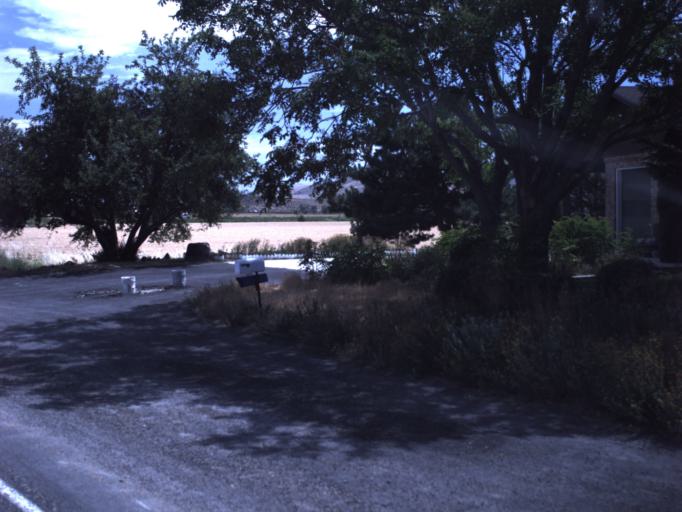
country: US
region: Utah
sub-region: Box Elder County
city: Tremonton
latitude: 41.6508
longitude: -112.3003
